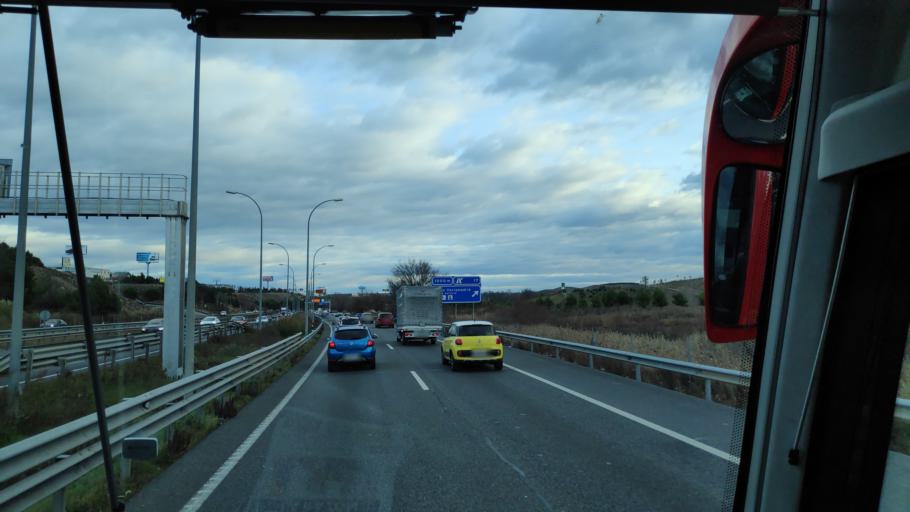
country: ES
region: Madrid
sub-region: Provincia de Madrid
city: Vaciamadrid
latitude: 40.3484
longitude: -3.5463
